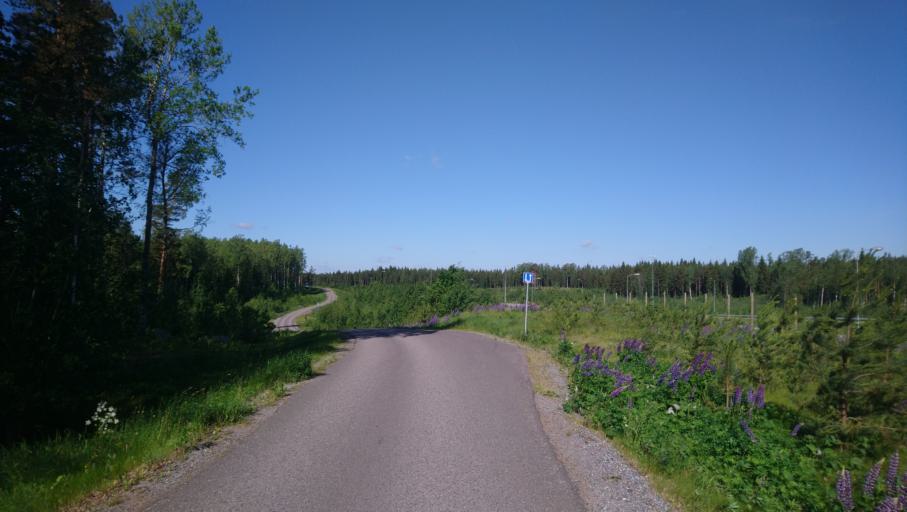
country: FI
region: Uusimaa
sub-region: Helsinki
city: Espoo
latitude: 60.1459
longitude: 24.5733
